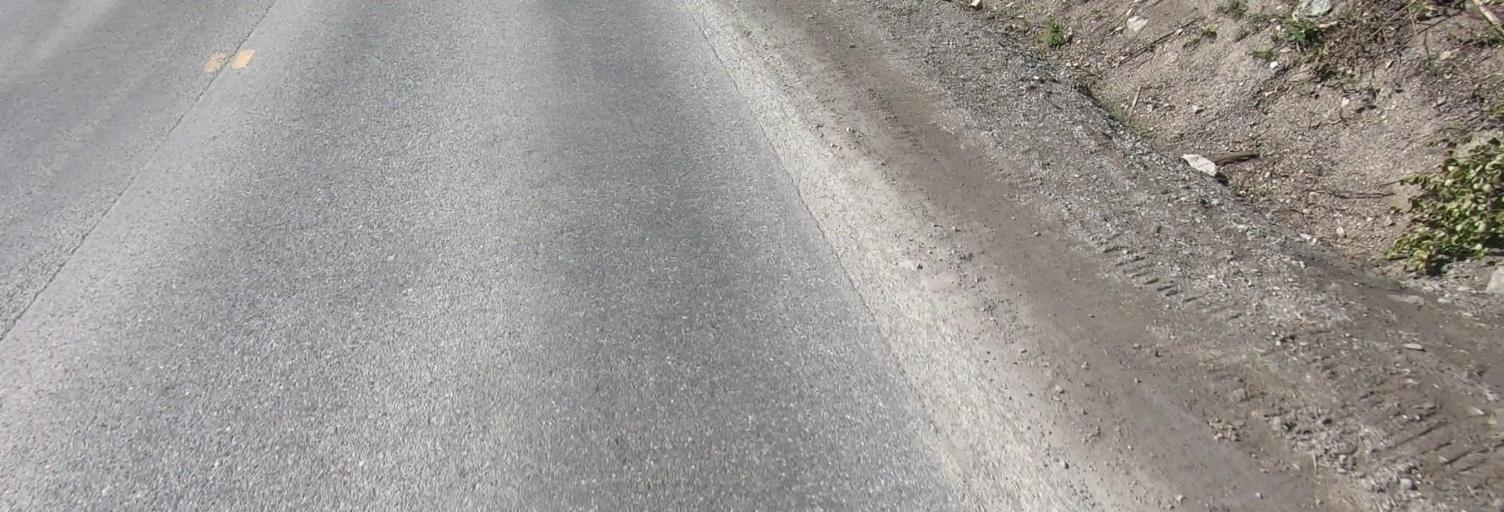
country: CA
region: British Columbia
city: Golden
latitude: 51.3045
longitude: -116.8712
